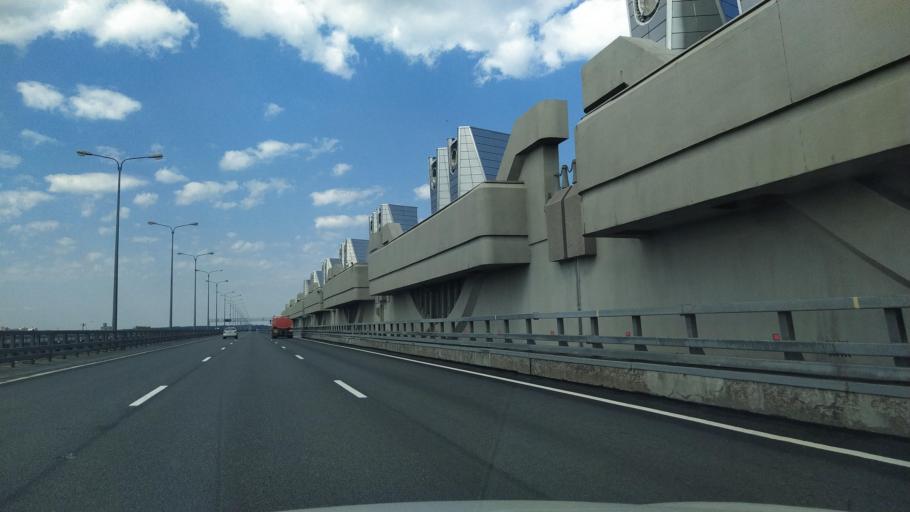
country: RU
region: St.-Petersburg
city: Kronshtadt
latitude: 60.0219
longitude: 29.7808
